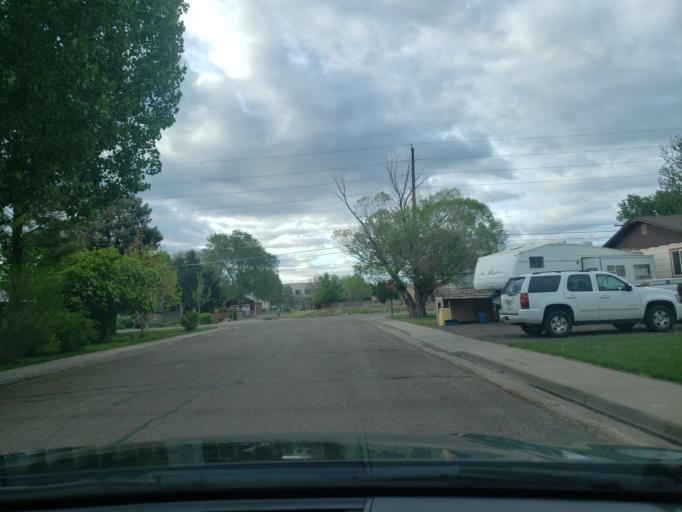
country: US
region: Colorado
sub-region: Mesa County
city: Fruita
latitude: 39.1602
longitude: -108.7371
